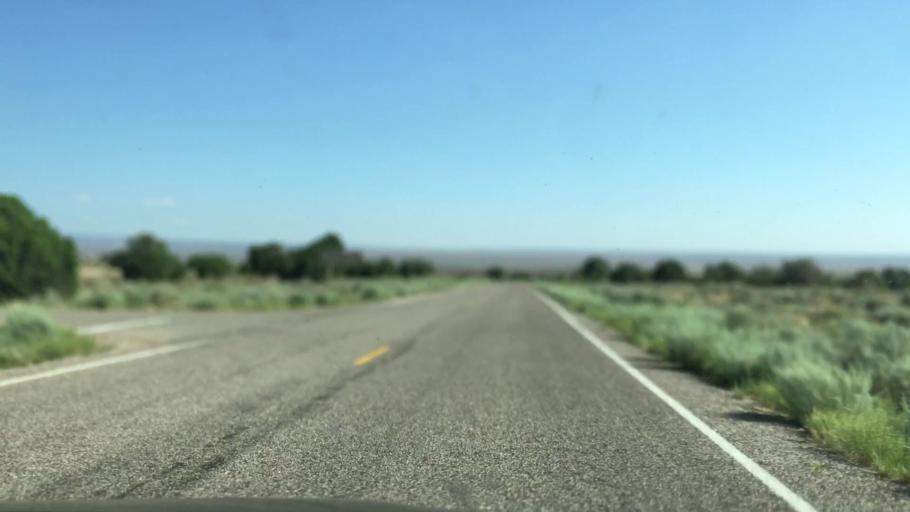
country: US
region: Arizona
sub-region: Coconino County
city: Fredonia
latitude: 36.8671
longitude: -112.7375
